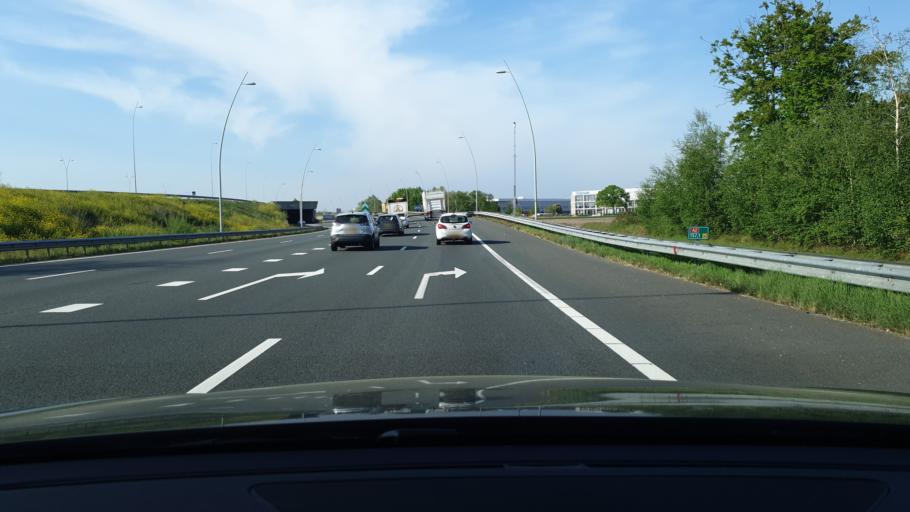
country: NL
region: North Brabant
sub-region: Gemeente Eindhoven
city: Meerhoven
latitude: 51.4720
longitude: 5.4061
